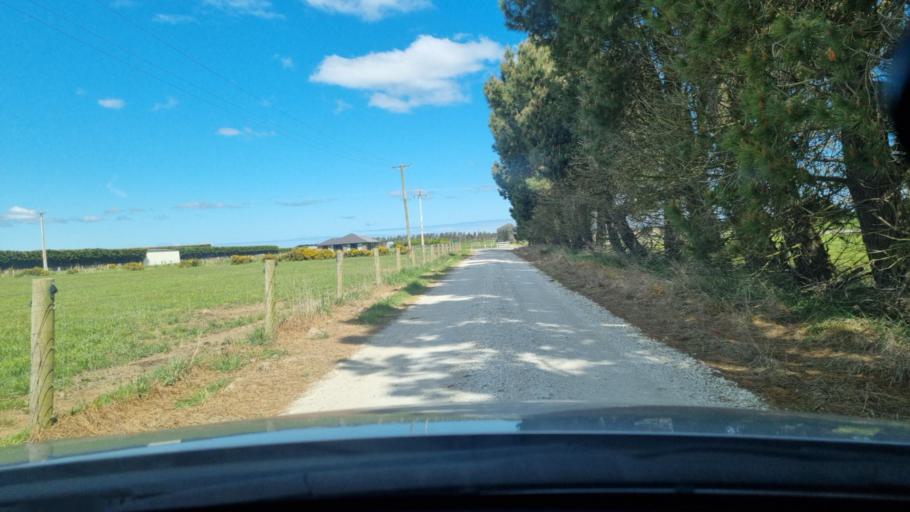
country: NZ
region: Southland
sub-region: Invercargill City
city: Invercargill
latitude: -46.3683
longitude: 168.2828
